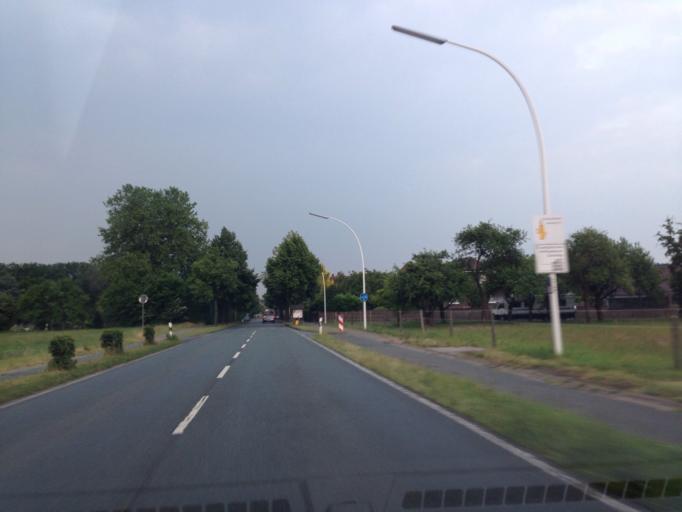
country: DE
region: North Rhine-Westphalia
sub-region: Regierungsbezirk Munster
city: Nottuln
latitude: 51.9025
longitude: 7.4163
